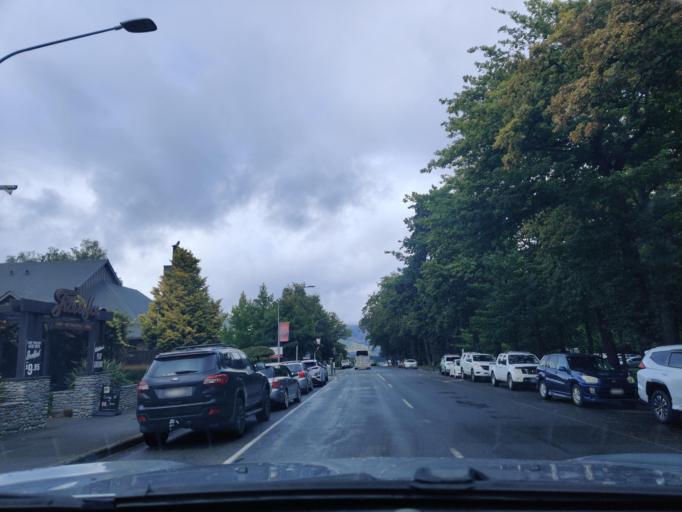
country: NZ
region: Canterbury
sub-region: Hurunui District
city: Amberley
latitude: -42.5232
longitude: 172.8297
